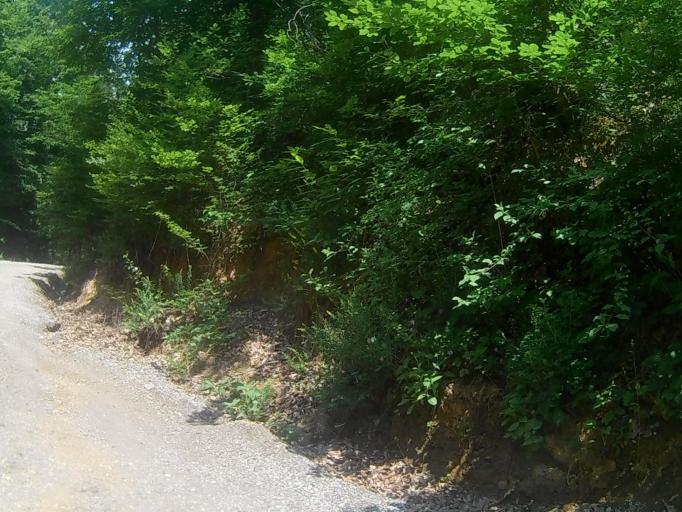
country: SI
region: Maribor
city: Bresternica
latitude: 46.5816
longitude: 15.5901
